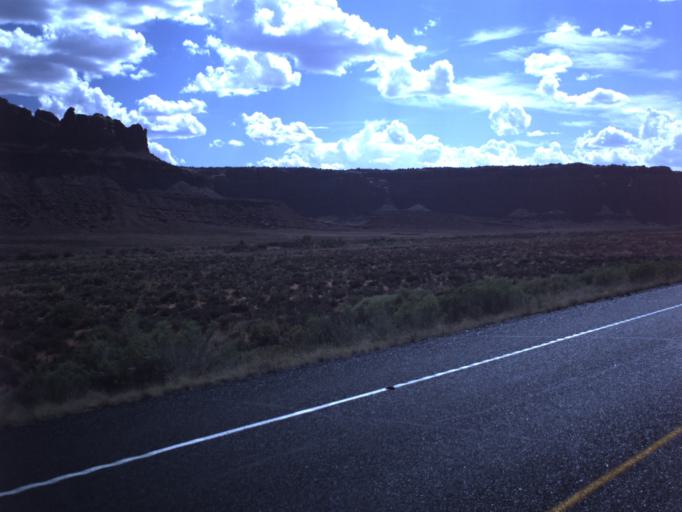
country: US
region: Utah
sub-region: Grand County
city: Moab
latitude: 38.6685
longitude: -109.6936
